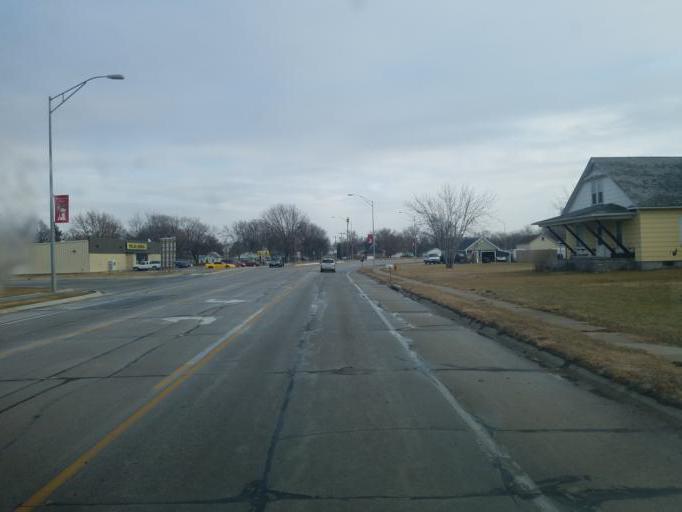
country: US
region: Nebraska
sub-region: Pierce County
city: Pierce
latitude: 42.1963
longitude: -97.5244
